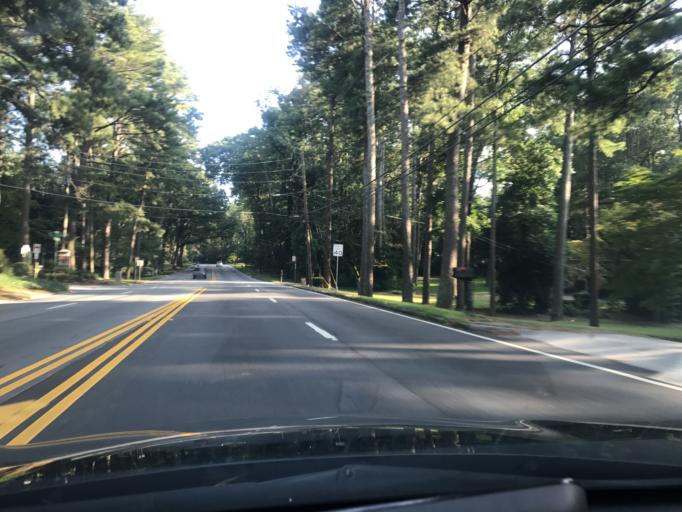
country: US
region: Georgia
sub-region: DeKalb County
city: North Druid Hills
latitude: 33.8253
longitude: -84.3073
